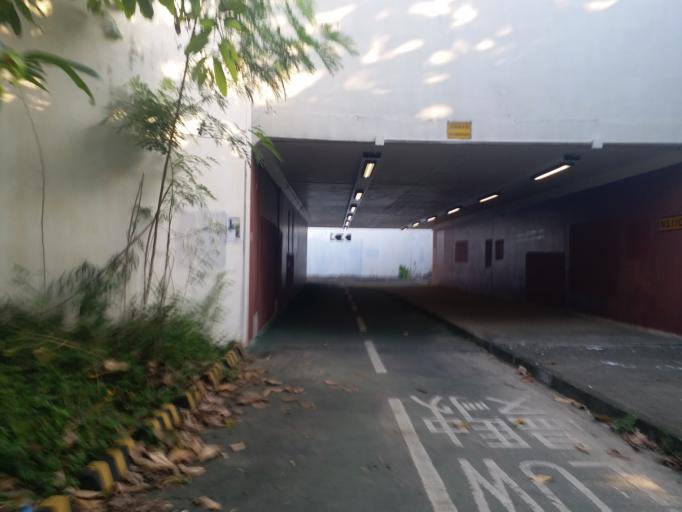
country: HK
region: Yuen Long
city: Yuen Long Kau Hui
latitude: 22.4443
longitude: 114.0479
